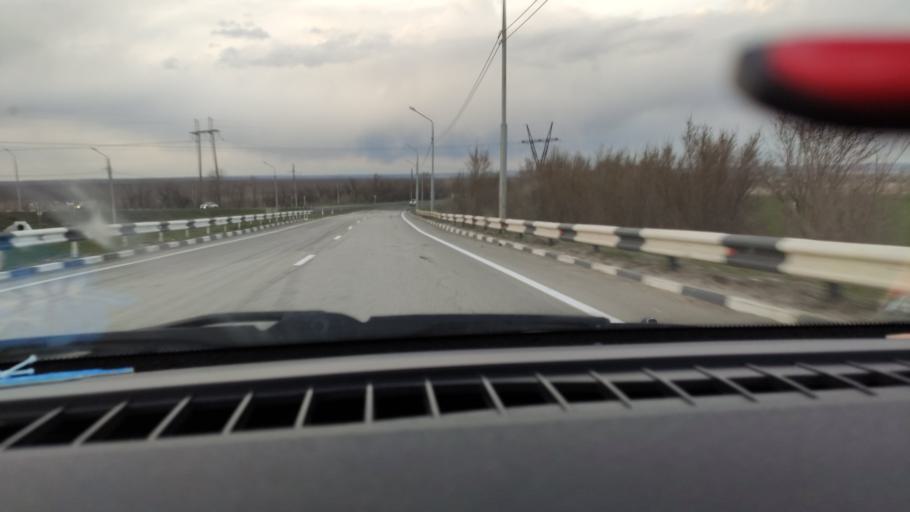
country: RU
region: Saratov
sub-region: Saratovskiy Rayon
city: Saratov
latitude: 51.6758
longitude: 46.0009
